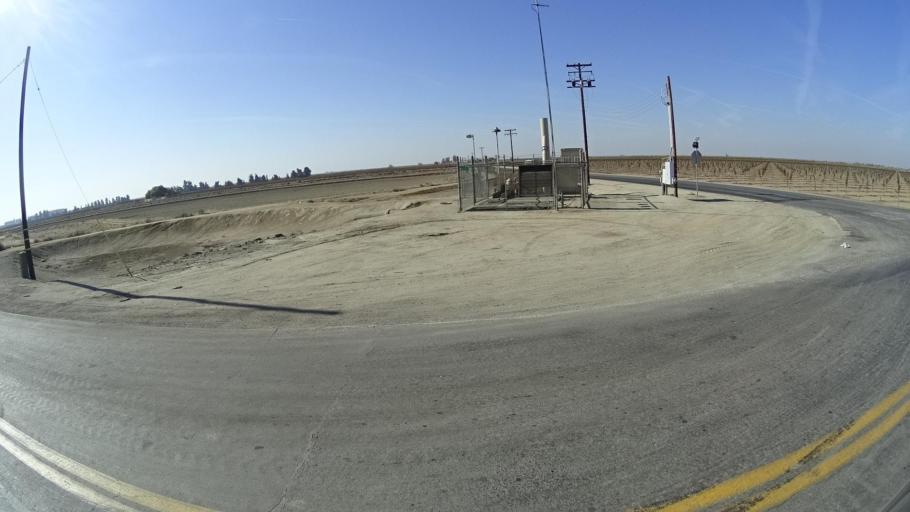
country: US
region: California
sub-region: Kern County
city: McFarland
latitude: 35.6454
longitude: -119.2045
